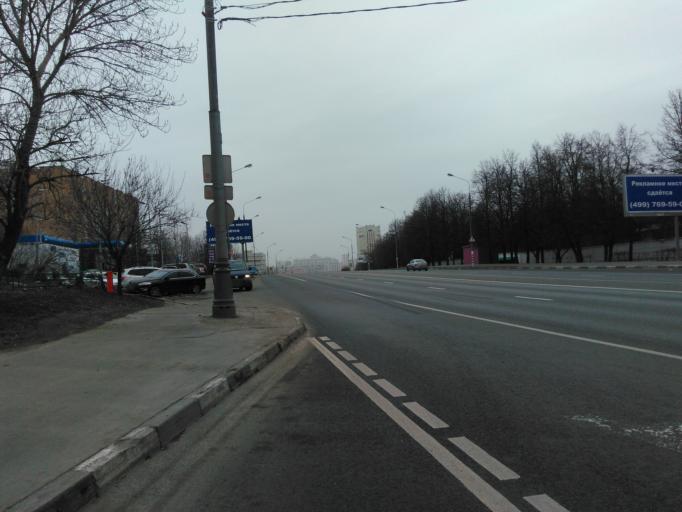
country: RU
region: Moskovskaya
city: Cheremushki
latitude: 55.6520
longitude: 37.5482
